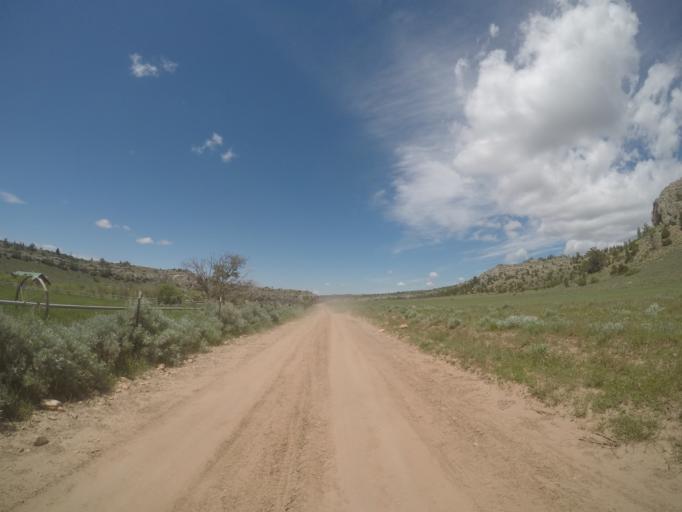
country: US
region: Montana
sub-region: Yellowstone County
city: Laurel
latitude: 45.2385
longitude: -108.6290
